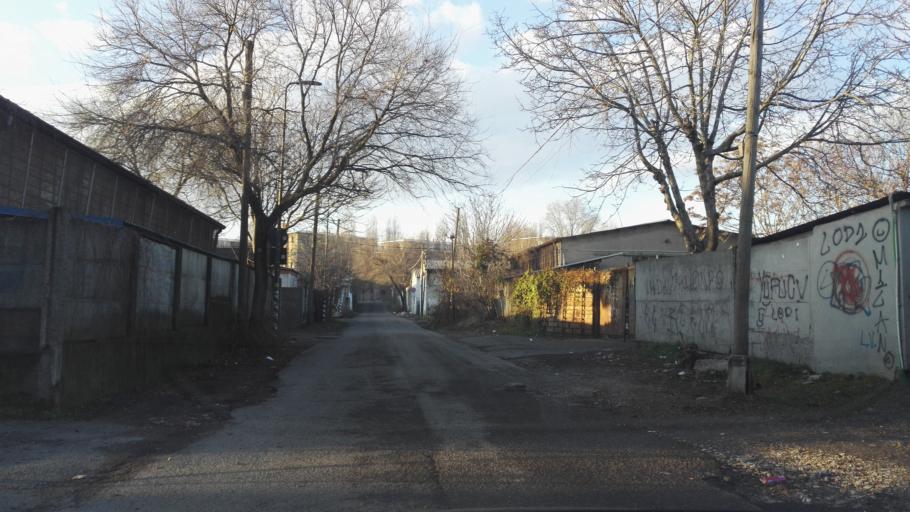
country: IT
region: Lombardy
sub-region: Citta metropolitana di Milano
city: Chiaravalle
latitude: 45.4343
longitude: 9.2296
